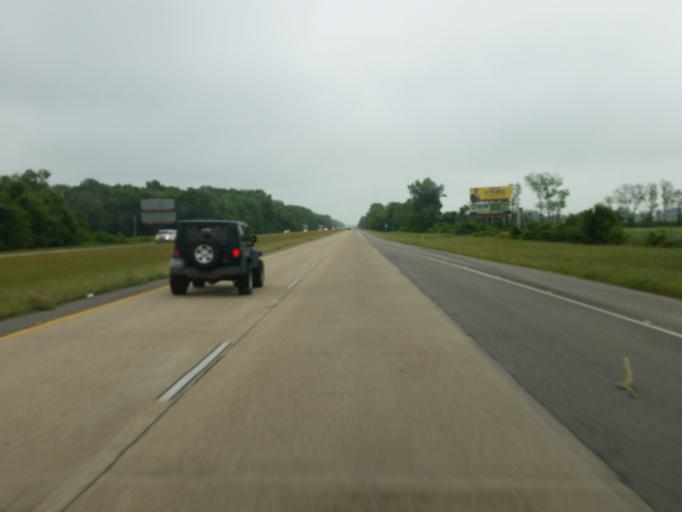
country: US
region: Louisiana
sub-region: Madison Parish
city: Tallulah
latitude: 32.3782
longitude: -91.1654
